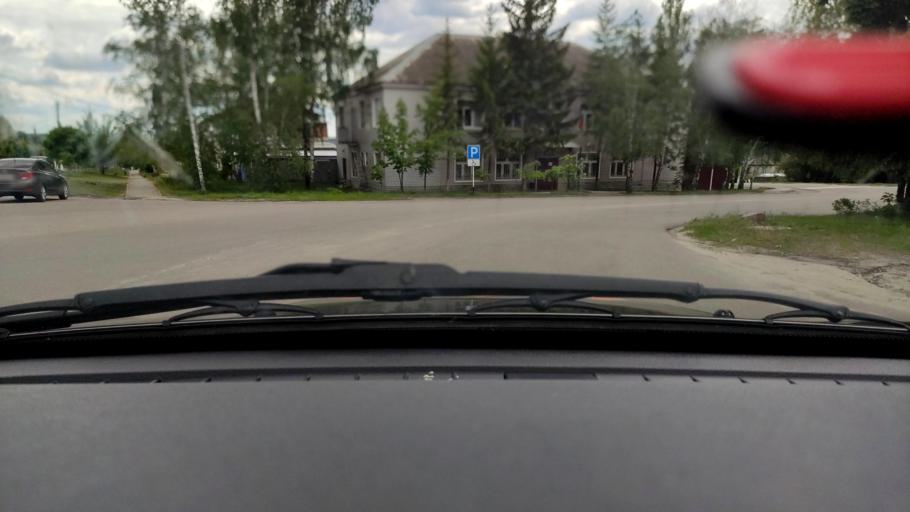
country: RU
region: Voronezj
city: Rossosh'
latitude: 51.0829
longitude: 38.6434
